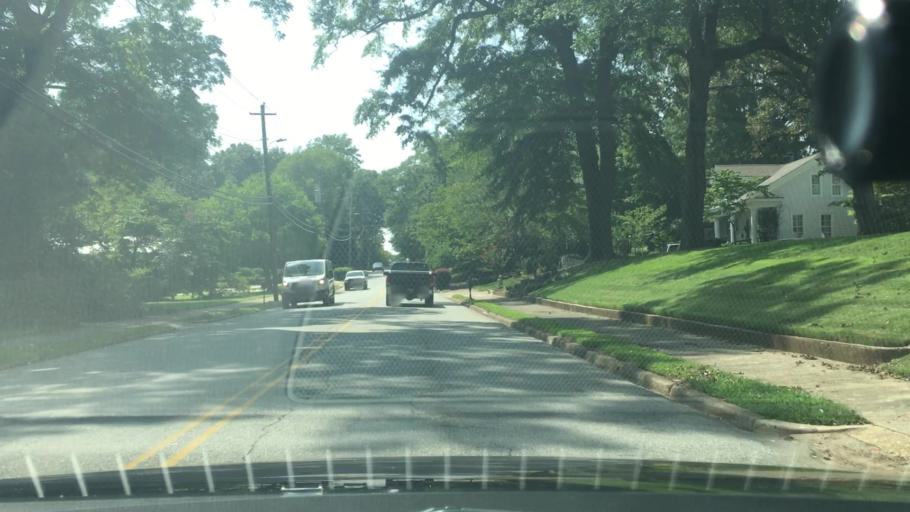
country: US
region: Georgia
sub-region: Coweta County
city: Newnan
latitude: 33.3738
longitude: -84.7923
